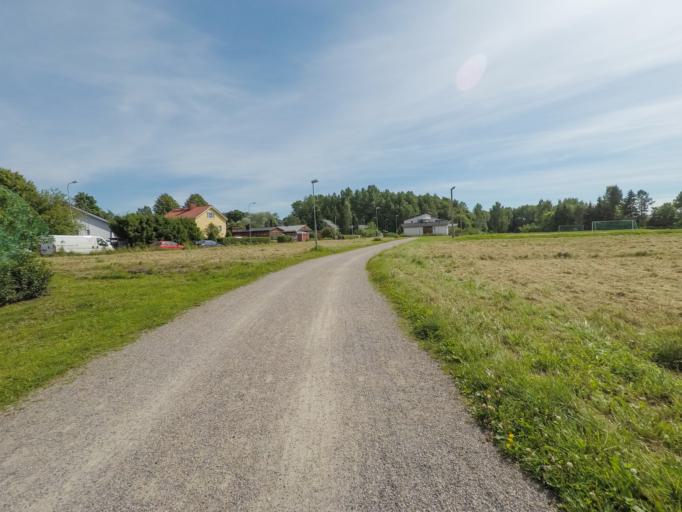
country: FI
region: Uusimaa
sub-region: Helsinki
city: Vantaa
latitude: 60.2605
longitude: 24.9770
